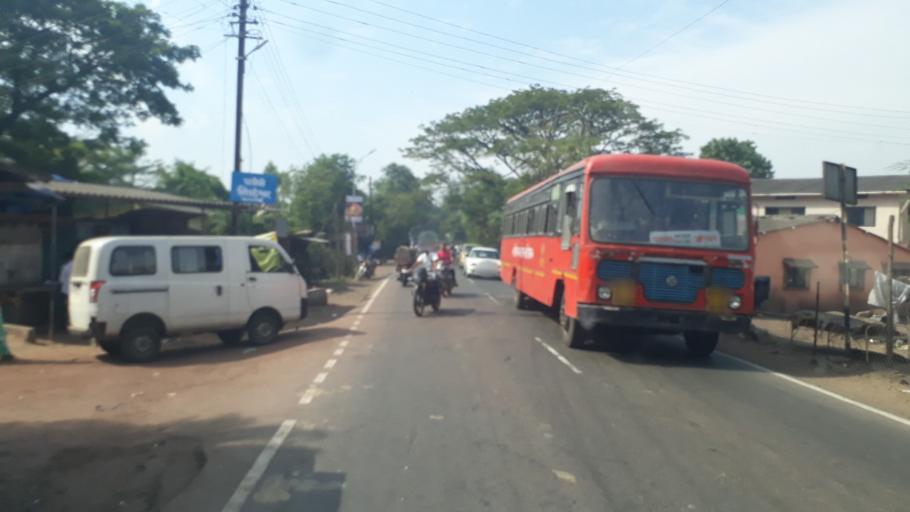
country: IN
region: Maharashtra
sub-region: Raigarh
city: Alibag
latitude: 18.6699
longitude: 72.9057
